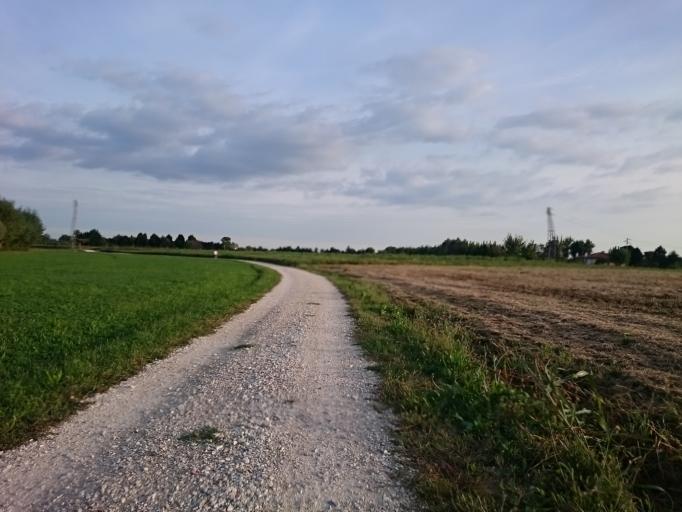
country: IT
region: Veneto
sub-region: Provincia di Vicenza
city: Camisano Vicentino
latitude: 45.5135
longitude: 11.7191
